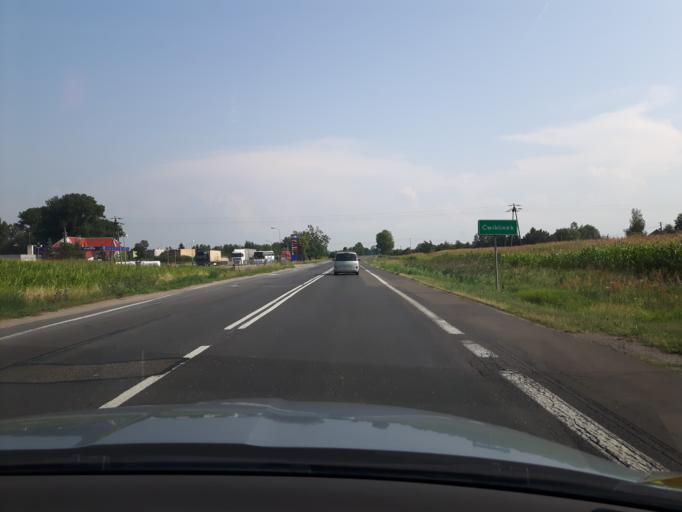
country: PL
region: Masovian Voivodeship
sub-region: Powiat plonski
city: Plonsk
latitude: 52.6794
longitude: 20.3664
